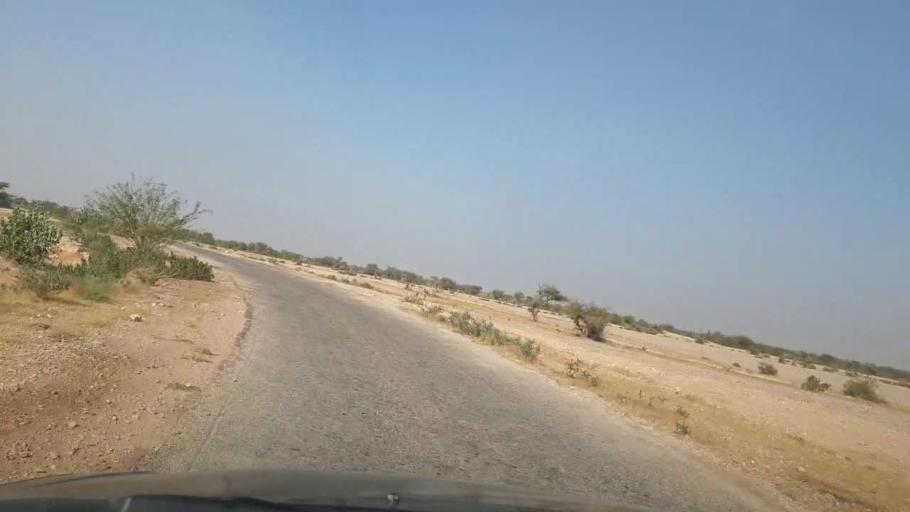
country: PK
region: Sindh
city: Jamshoro
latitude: 25.5535
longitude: 67.8290
